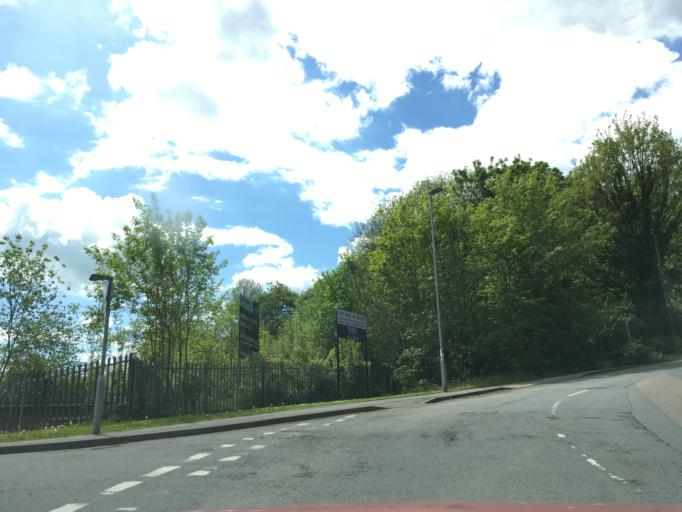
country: GB
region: England
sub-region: Gloucestershire
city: Dursley
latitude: 51.6898
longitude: -2.3556
